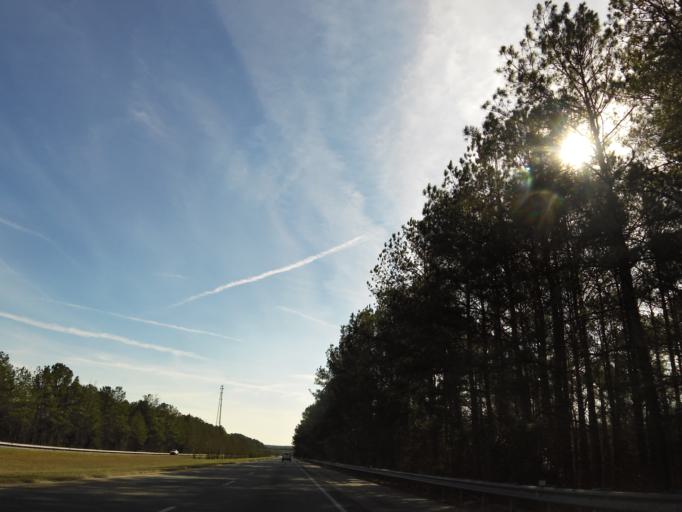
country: US
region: Georgia
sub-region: Harris County
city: Pine Mountain
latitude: 32.9168
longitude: -84.9473
